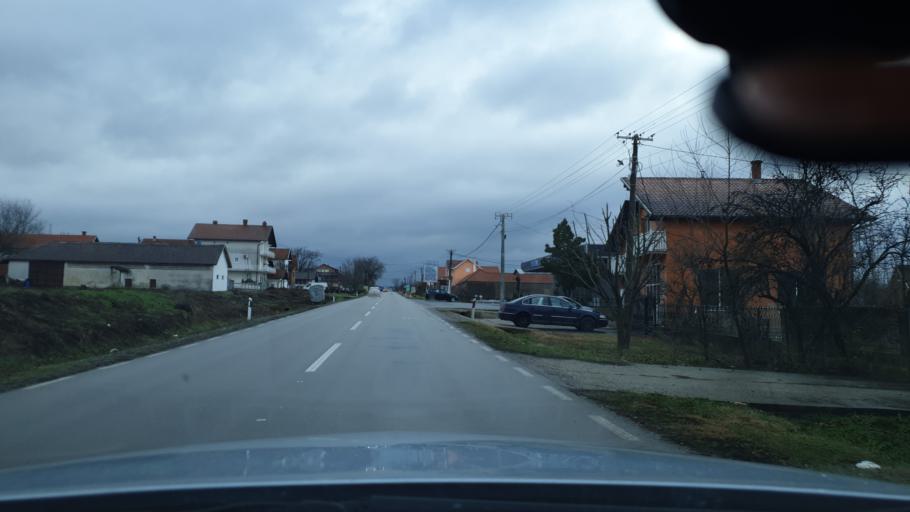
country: RS
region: Central Serbia
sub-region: Branicevski Okrug
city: Petrovac
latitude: 44.4240
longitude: 21.3692
